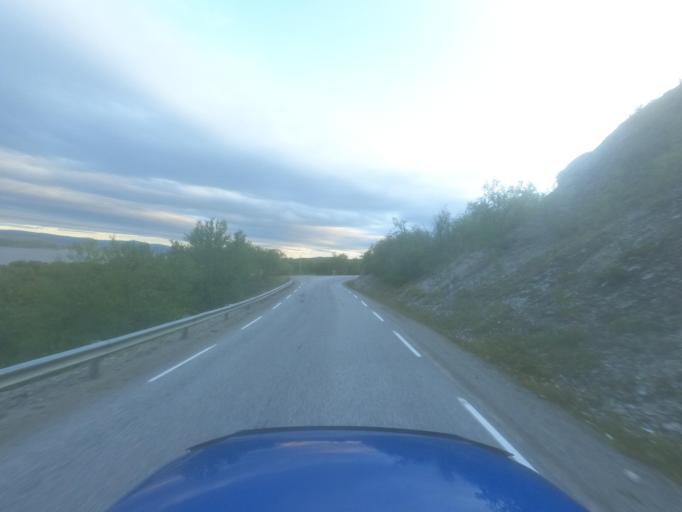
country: NO
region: Finnmark Fylke
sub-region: Porsanger
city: Lakselv
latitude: 70.2573
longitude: 25.0215
